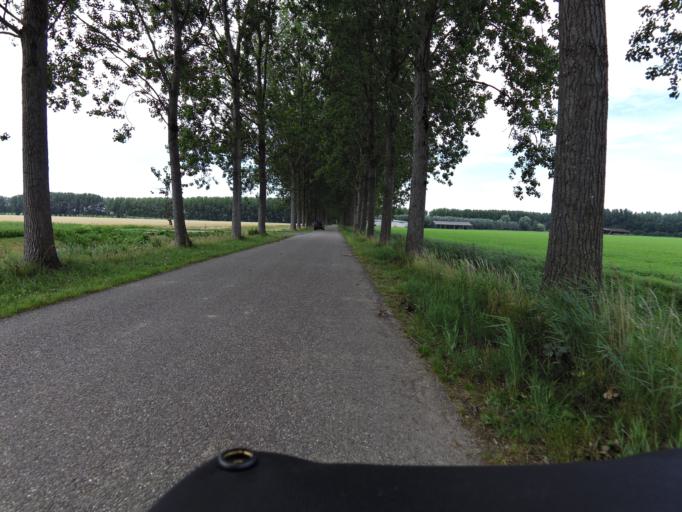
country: NL
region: North Brabant
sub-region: Gemeente Moerdijk
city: Willemstad
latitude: 51.7202
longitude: 4.4842
